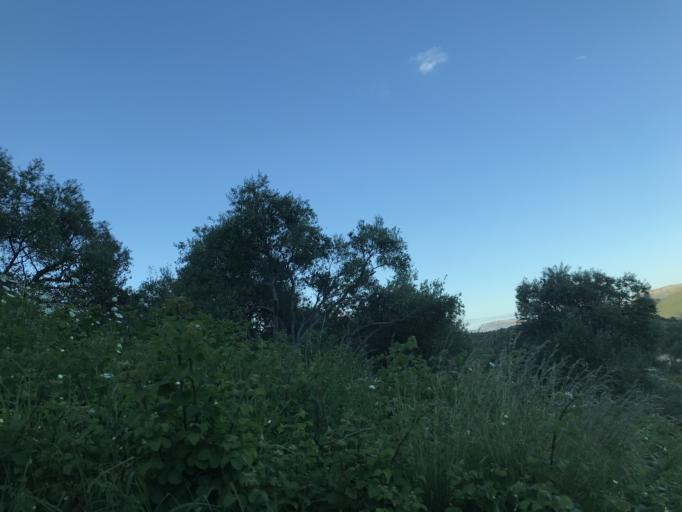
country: TR
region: Hatay
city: Buyukcat
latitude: 36.0988
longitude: 36.0648
